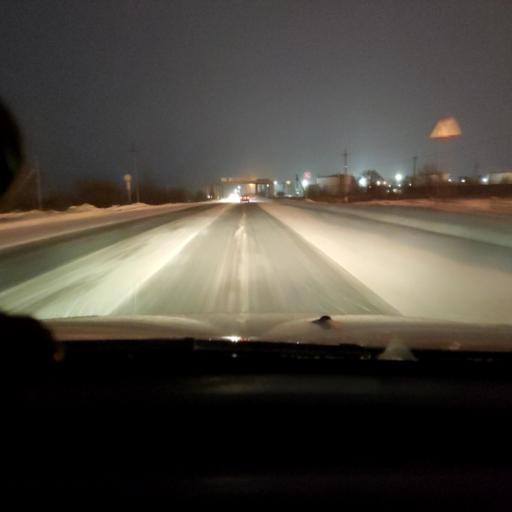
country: RU
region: Samara
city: Otradnyy
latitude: 53.3473
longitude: 51.3113
